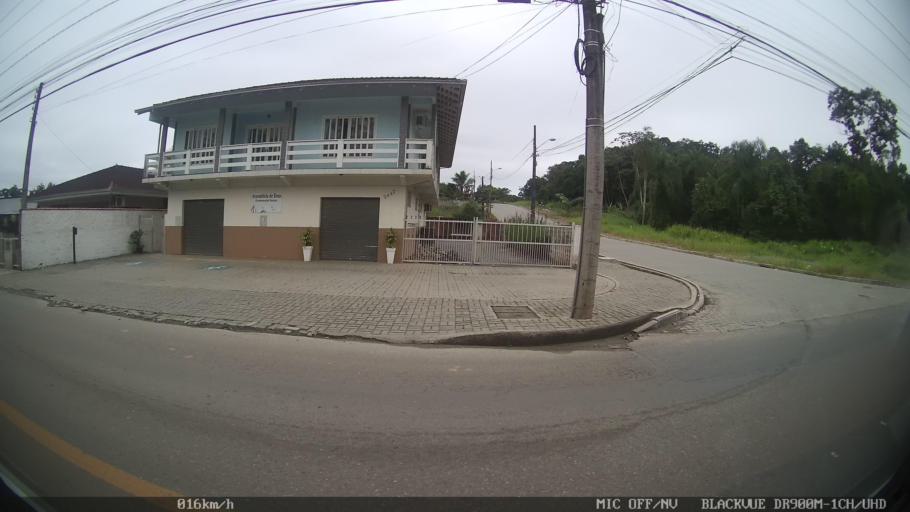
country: BR
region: Santa Catarina
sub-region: Joinville
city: Joinville
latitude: -26.2778
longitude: -48.9128
